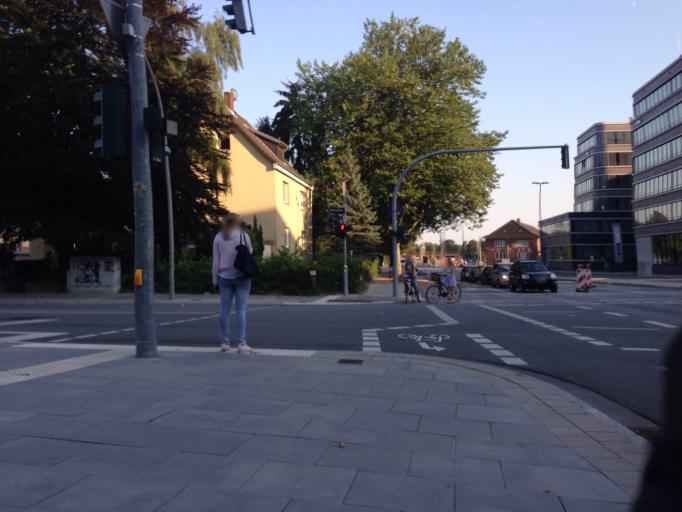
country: DE
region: Hamburg
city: Marienthal
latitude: 53.5692
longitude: 10.0619
